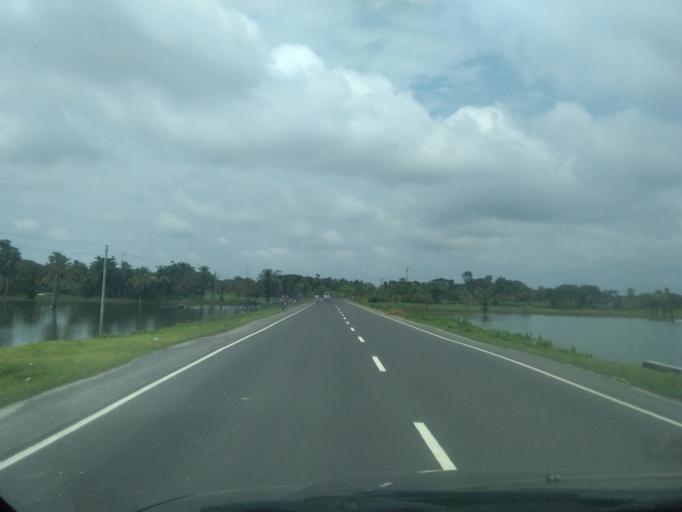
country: BD
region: Khulna
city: Kesabpur
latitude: 22.7830
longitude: 89.2091
